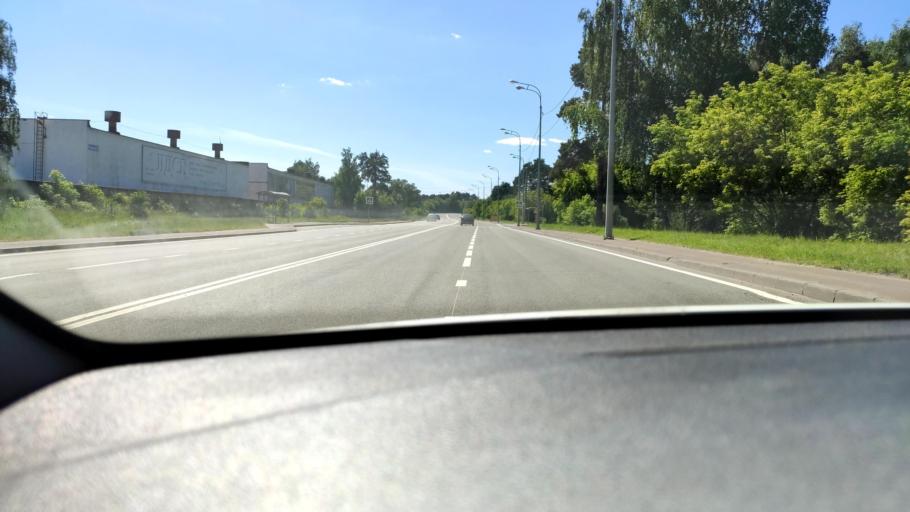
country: RU
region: Tatarstan
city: Staroye Arakchino
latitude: 55.8369
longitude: 49.0312
